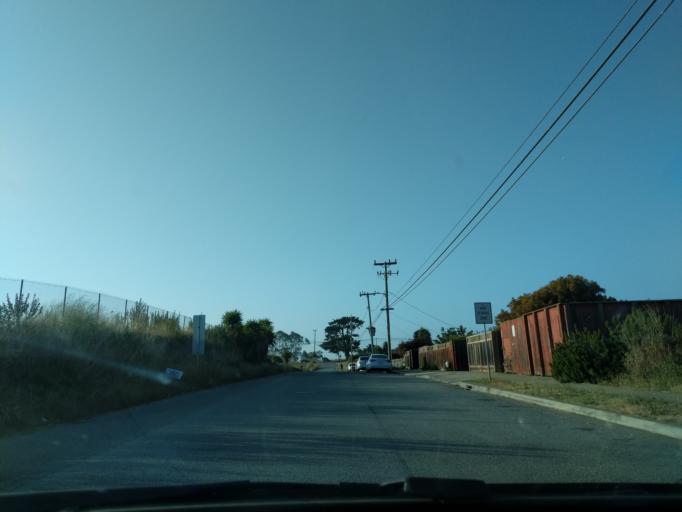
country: US
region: California
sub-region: Monterey County
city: Las Lomas
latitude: 36.8707
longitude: -121.7626
